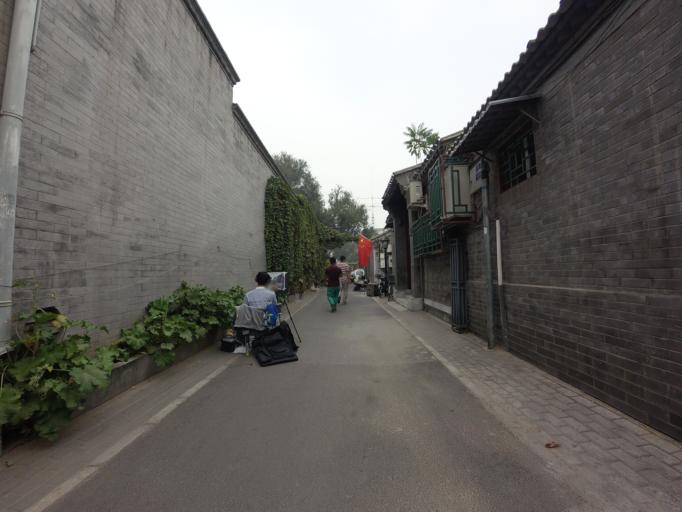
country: CN
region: Beijing
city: Jingshan
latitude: 39.9374
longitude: 116.3820
